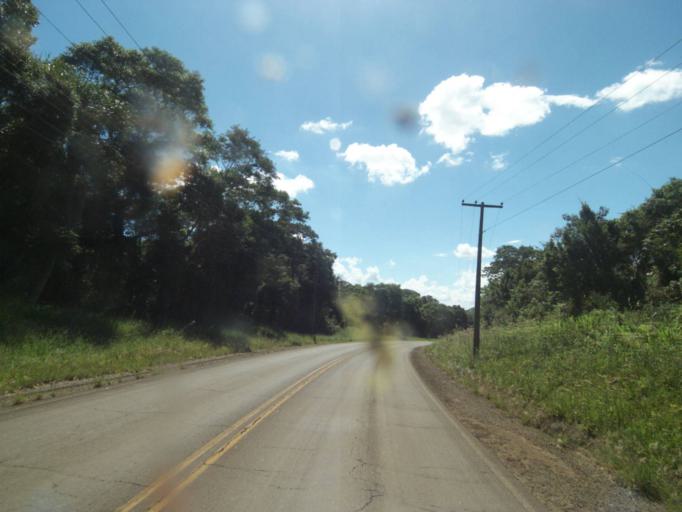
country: BR
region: Parana
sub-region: Chopinzinho
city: Chopinzinho
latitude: -25.7862
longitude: -52.0988
